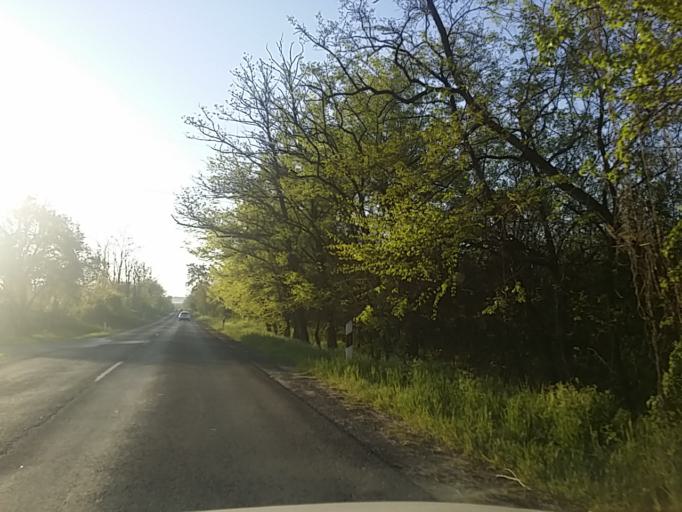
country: HU
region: Pest
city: Fot
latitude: 47.6029
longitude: 19.2093
